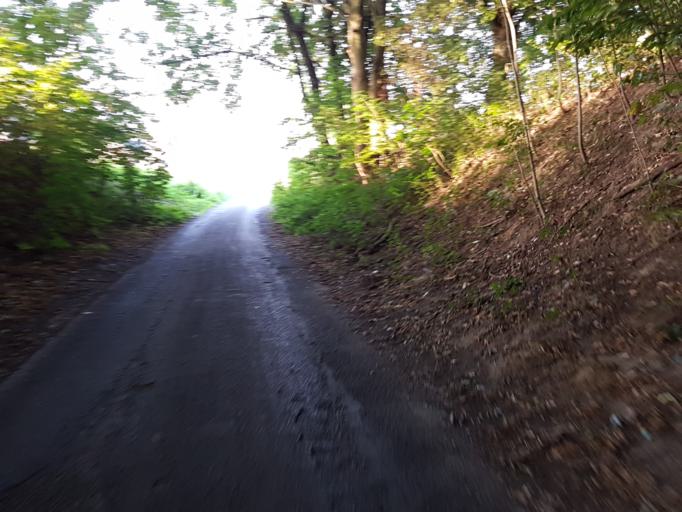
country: BE
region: Flanders
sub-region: Provincie Vlaams-Brabant
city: Vilvoorde
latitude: 50.9184
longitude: 4.4084
